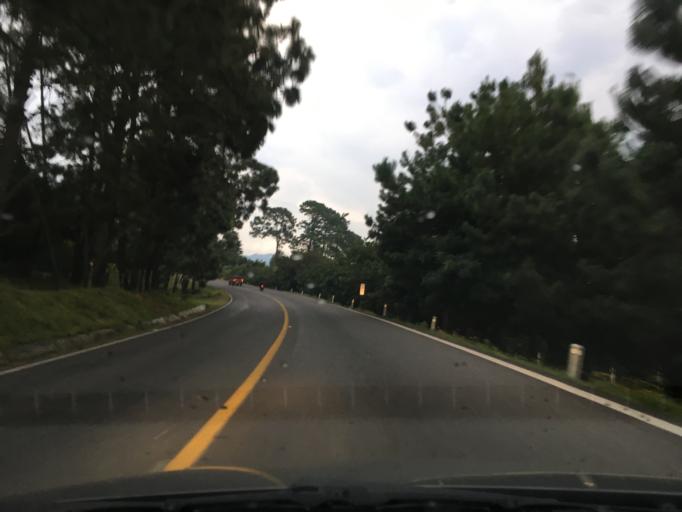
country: MX
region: Michoacan
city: Tingambato
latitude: 19.4830
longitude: -101.8890
